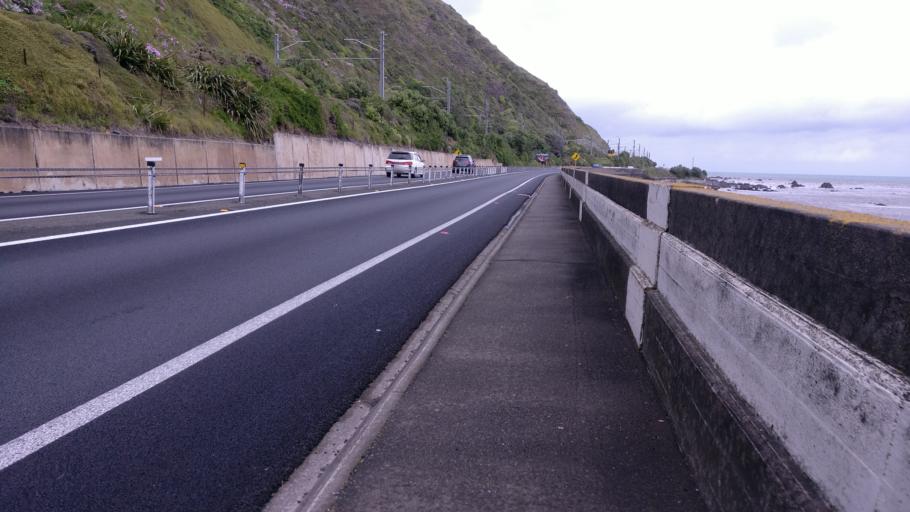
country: NZ
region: Wellington
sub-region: Kapiti Coast District
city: Paraparaumu
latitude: -41.0031
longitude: 174.9338
